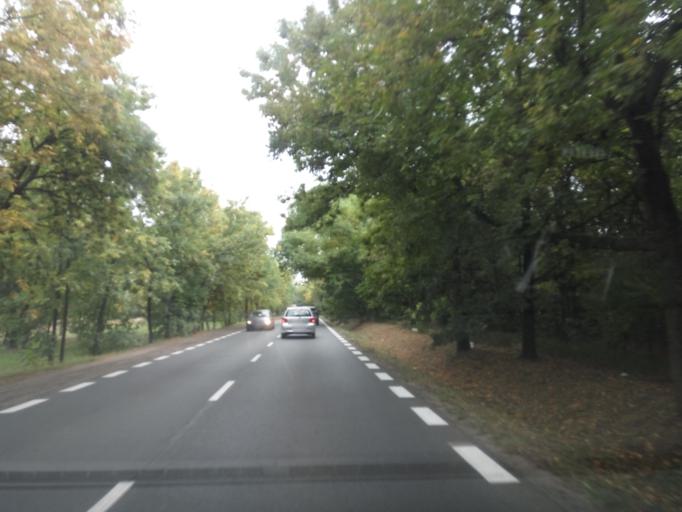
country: PL
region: Lower Silesian Voivodeship
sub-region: Powiat wroclawski
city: Radwanice
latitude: 51.0721
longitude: 17.0782
